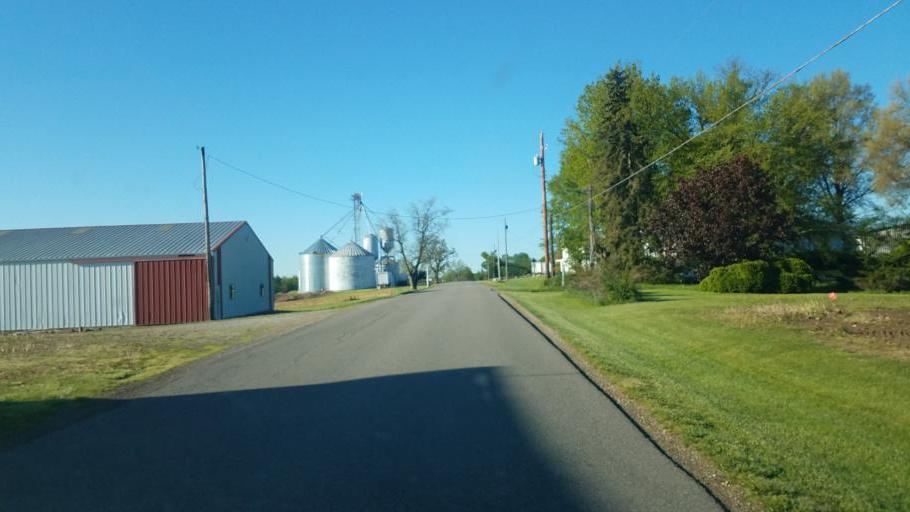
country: US
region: Ohio
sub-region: Morrow County
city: Cardington
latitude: 40.3910
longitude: -82.8127
